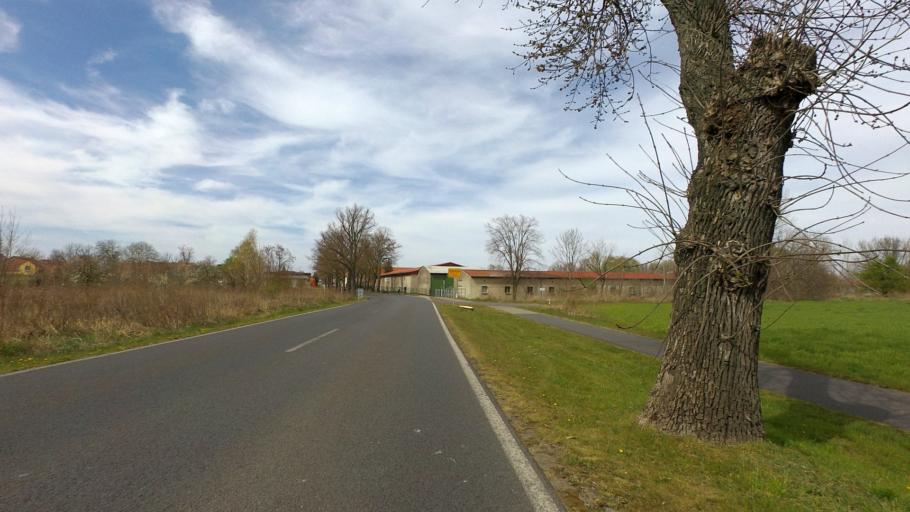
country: DE
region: Berlin
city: Lichtenrade
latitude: 52.3785
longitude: 13.4495
